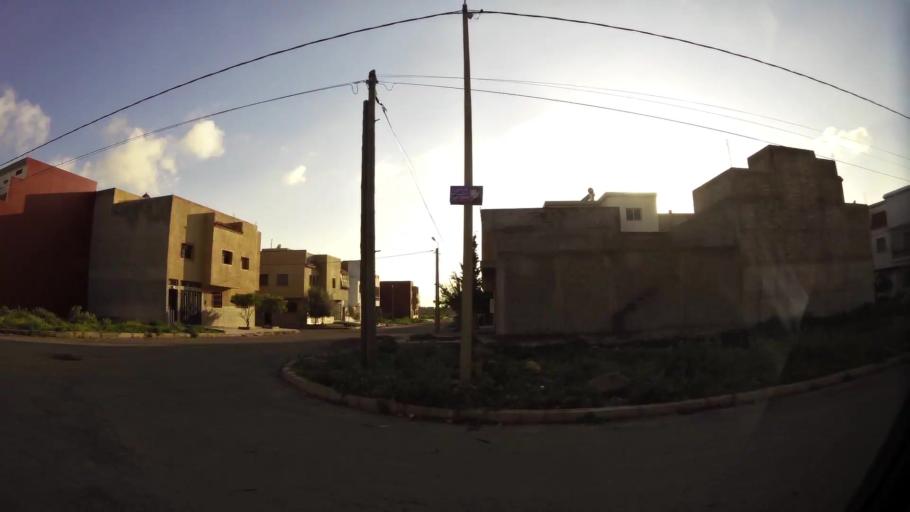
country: MA
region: Chaouia-Ouardigha
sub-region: Settat Province
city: Settat
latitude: 33.0096
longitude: -7.5967
